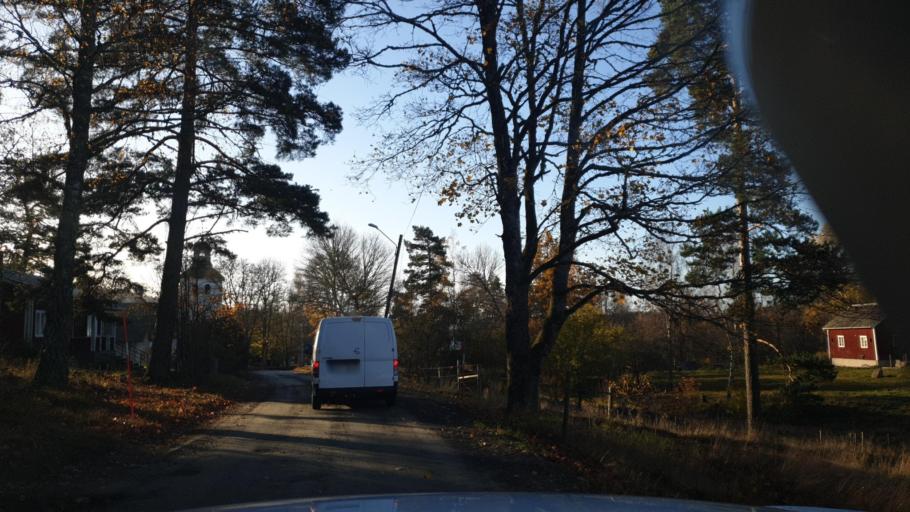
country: SE
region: Vaermland
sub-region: Grums Kommun
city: Slottsbron
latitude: 59.4566
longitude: 12.9172
